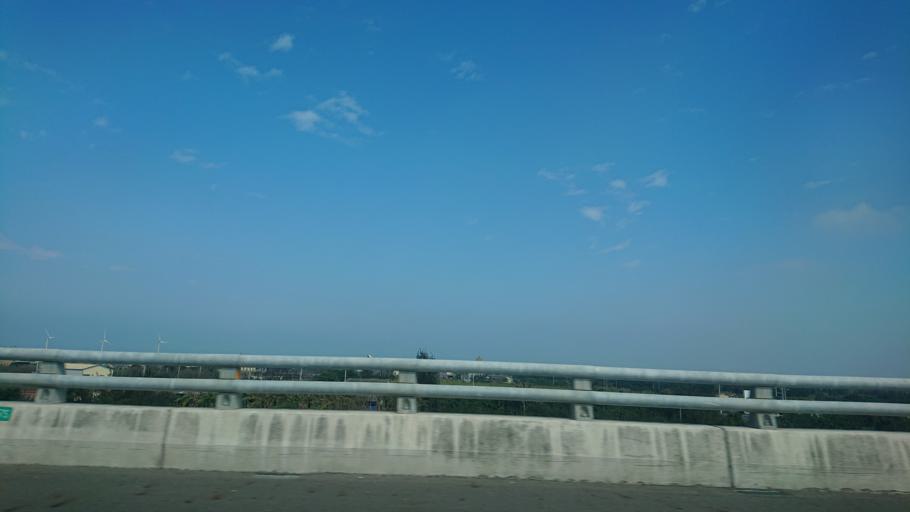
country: TW
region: Taiwan
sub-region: Changhua
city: Chang-hua
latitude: 23.9706
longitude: 120.3525
